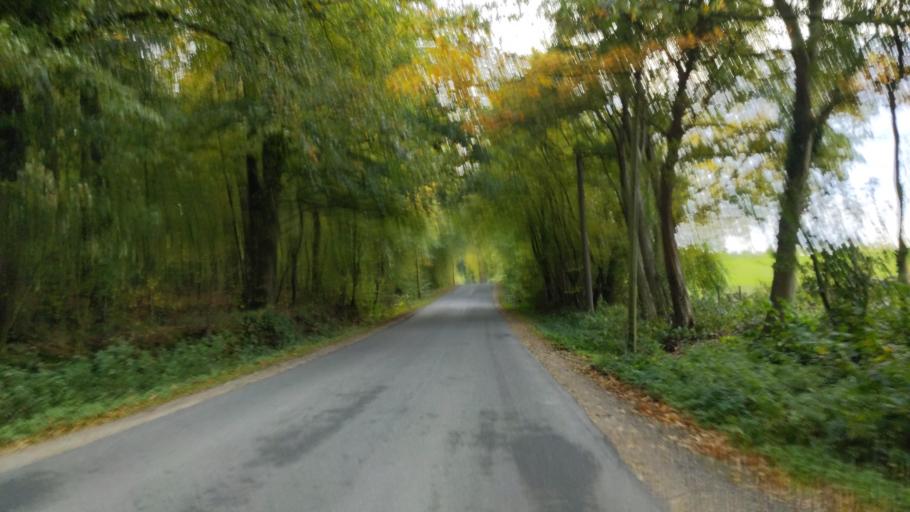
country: DE
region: Schleswig-Holstein
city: Susel
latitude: 54.0500
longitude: 10.7174
